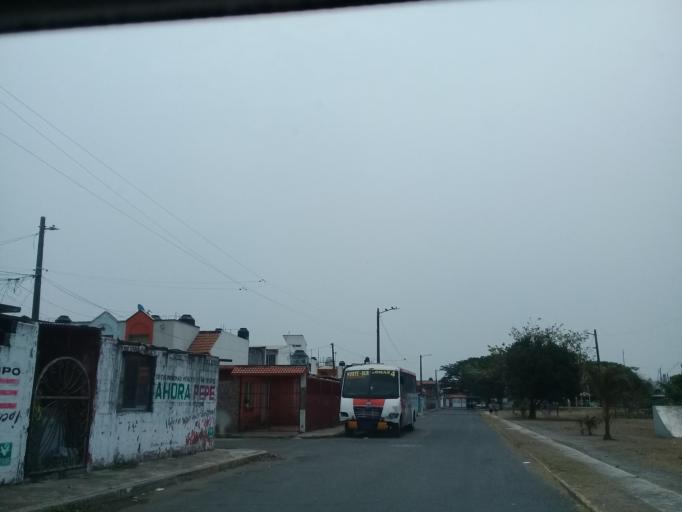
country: MX
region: Veracruz
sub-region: Veracruz
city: Rio Medio [Granja]
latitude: 19.2107
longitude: -96.2028
